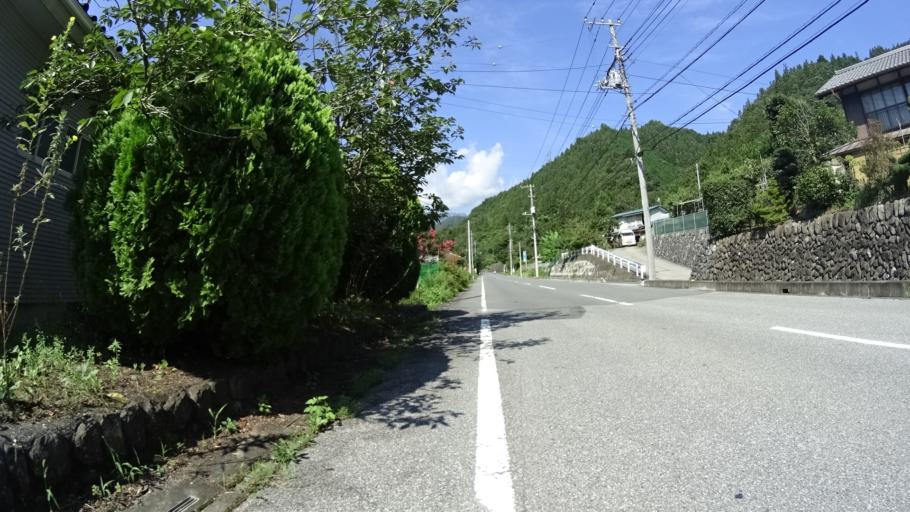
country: JP
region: Saitama
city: Chichibu
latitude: 36.0338
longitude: 138.9350
